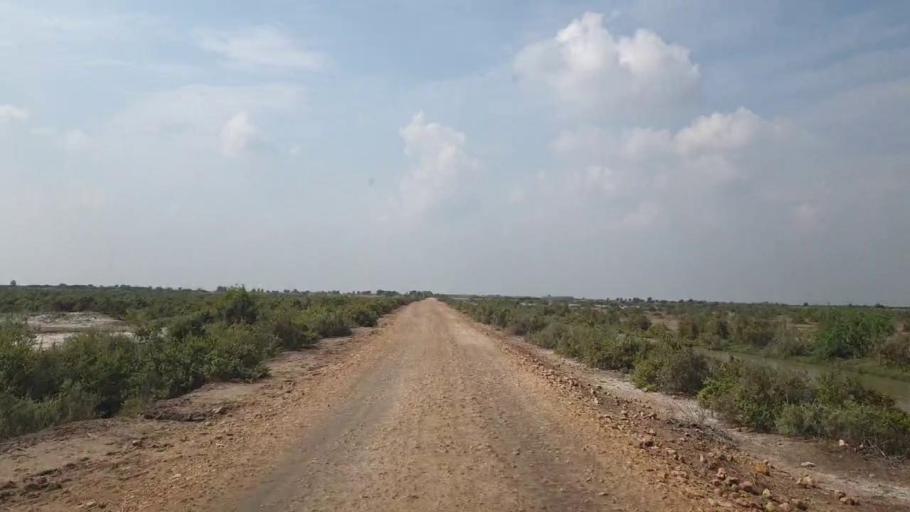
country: PK
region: Sindh
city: Badin
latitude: 24.5066
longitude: 68.6124
